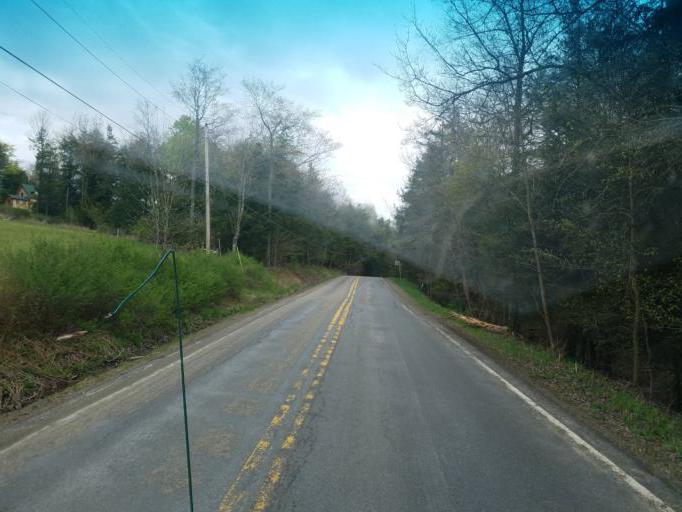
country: US
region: Pennsylvania
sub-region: Tioga County
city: Wellsboro
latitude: 41.6972
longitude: -77.4356
